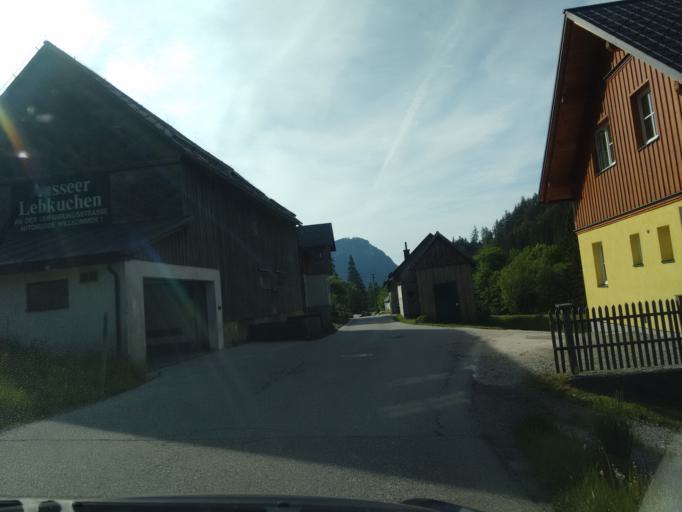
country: AT
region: Styria
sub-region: Politischer Bezirk Liezen
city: Altaussee
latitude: 47.6505
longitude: 13.7537
